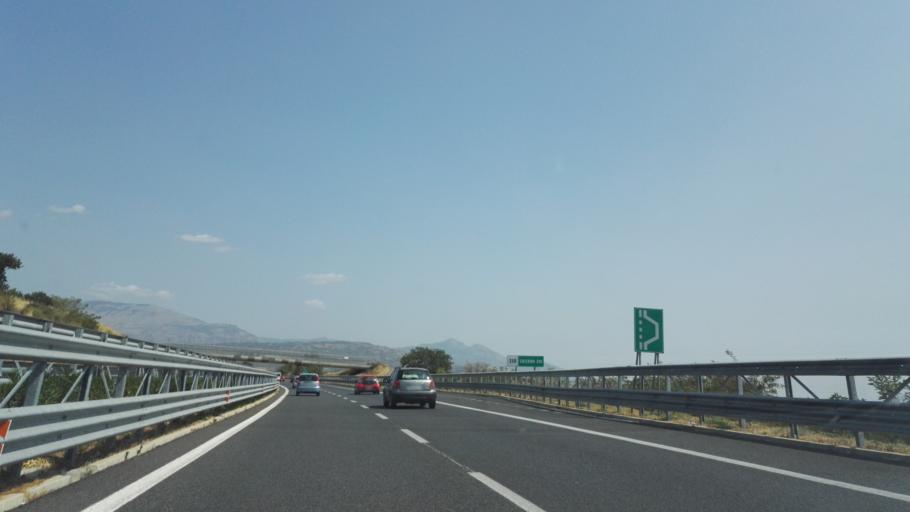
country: IT
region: Calabria
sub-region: Provincia di Cosenza
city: San Lorenzo del Vallo
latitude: 39.7050
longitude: 16.2427
